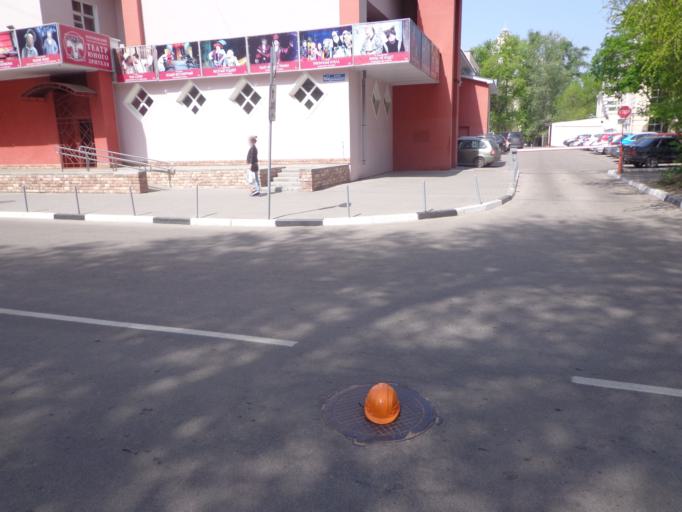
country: RU
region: Voronezj
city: Voronezh
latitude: 51.6609
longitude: 39.2048
